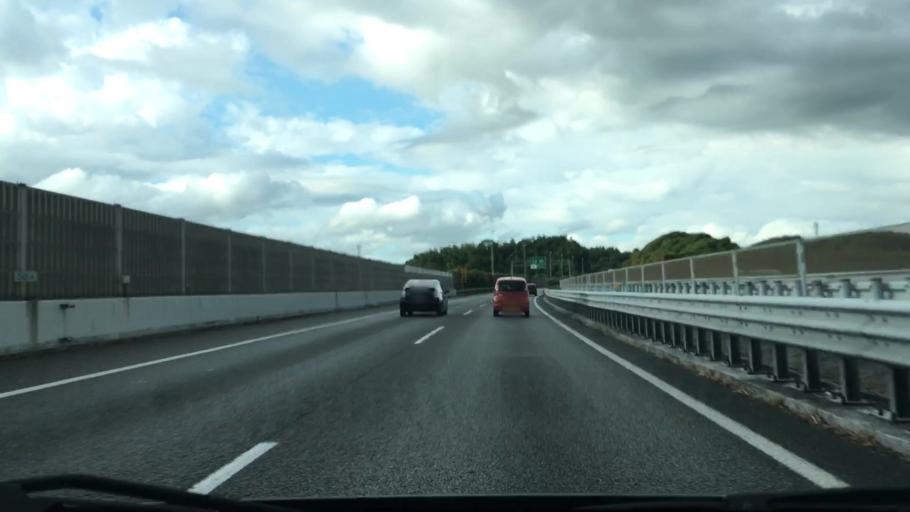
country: JP
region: Fukuoka
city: Koga
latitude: 33.7141
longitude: 130.4903
